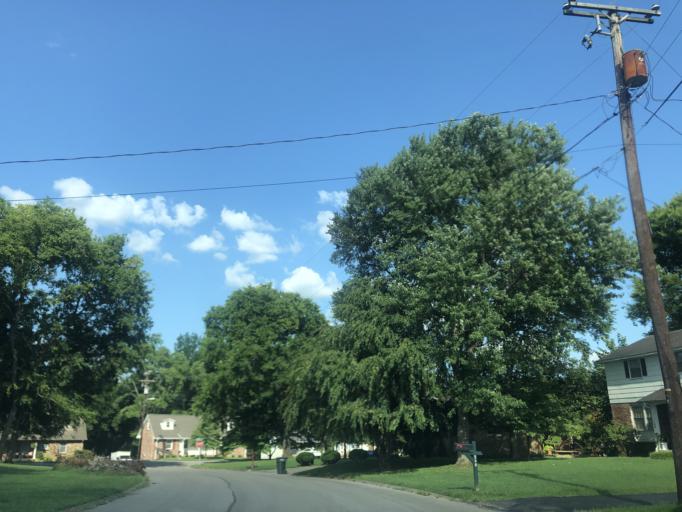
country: US
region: Tennessee
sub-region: Wilson County
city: Green Hill
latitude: 36.2064
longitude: -86.5978
